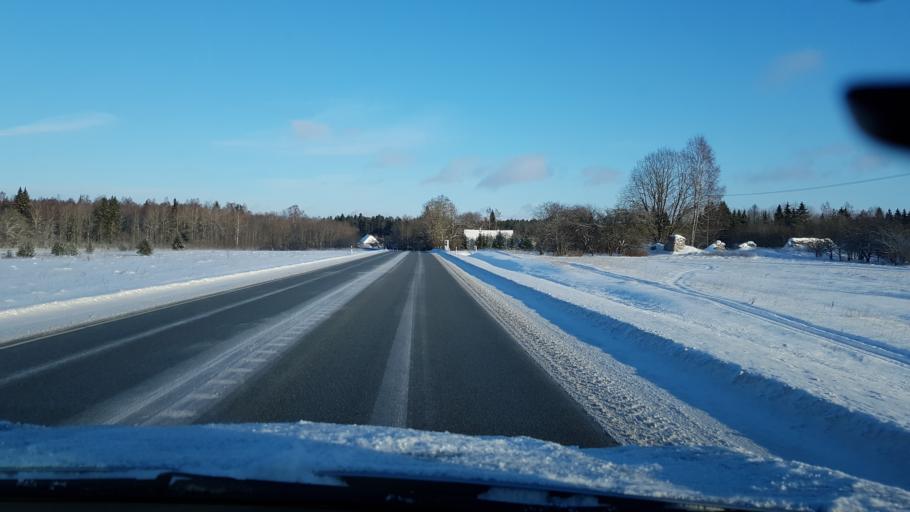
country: EE
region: Harju
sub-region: Keila linn
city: Keila
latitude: 59.2290
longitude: 24.4551
